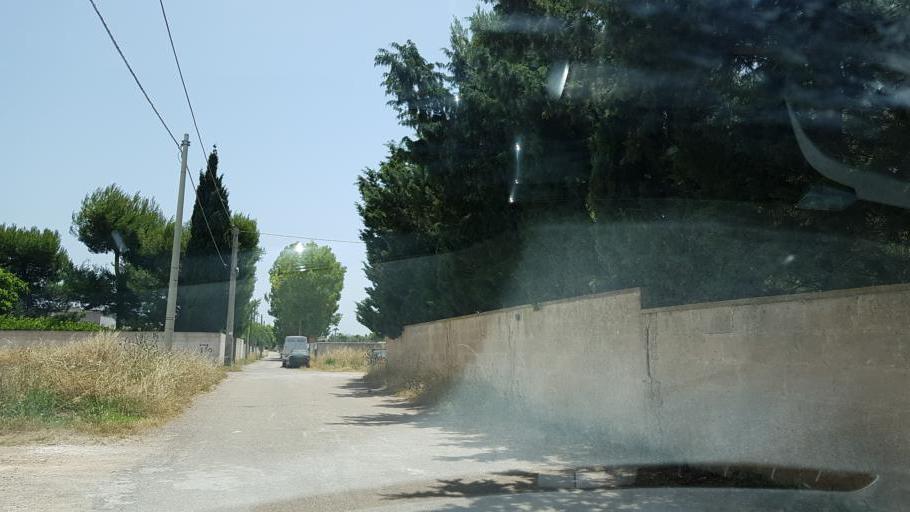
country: IT
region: Apulia
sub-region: Provincia di Lecce
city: Porto Cesareo
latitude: 40.2520
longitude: 17.9203
